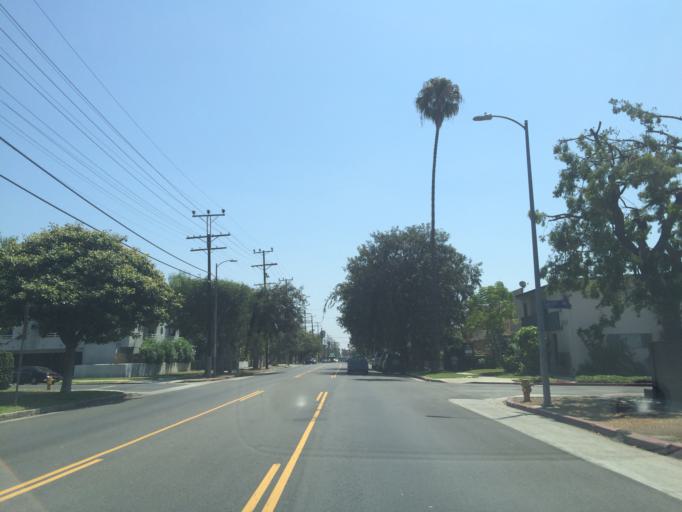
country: US
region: California
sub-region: Los Angeles County
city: Culver City
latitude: 34.0313
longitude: -118.3984
